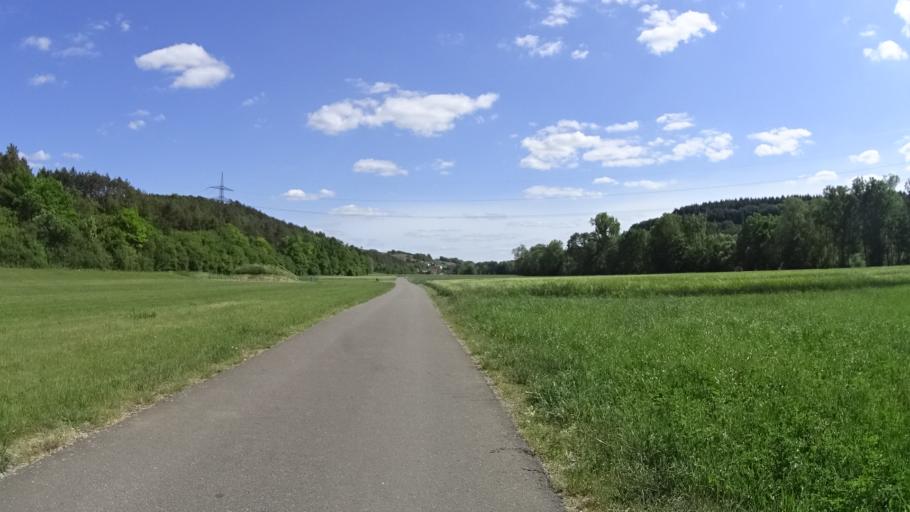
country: DE
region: Baden-Wuerttemberg
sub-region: Karlsruhe Region
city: Hardheim
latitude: 49.5926
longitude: 9.4806
